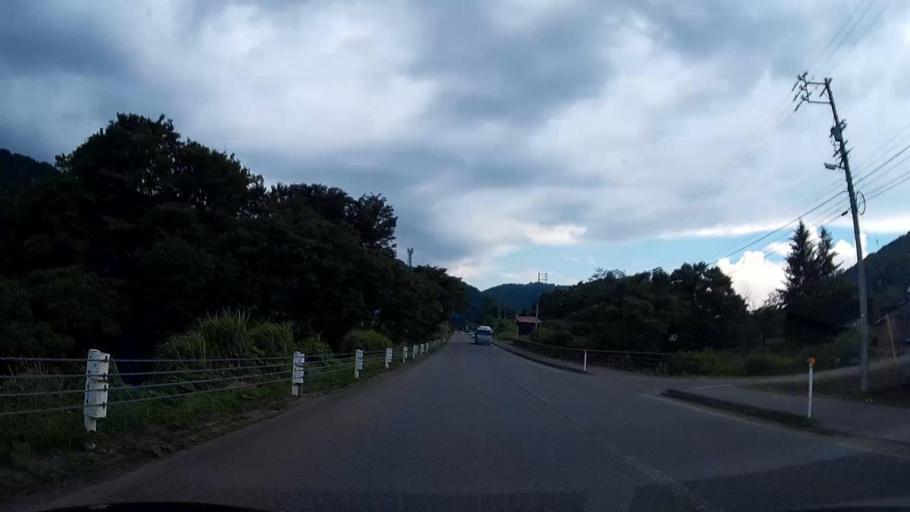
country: JP
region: Nagano
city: Iiyama
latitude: 36.9846
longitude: 138.5063
